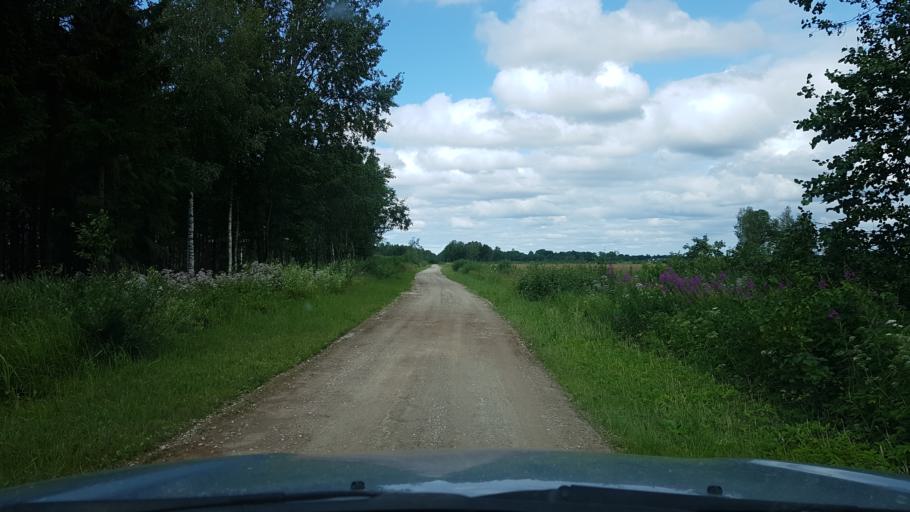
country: EE
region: Ida-Virumaa
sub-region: Narva-Joesuu linn
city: Narva-Joesuu
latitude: 59.3647
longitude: 27.9230
